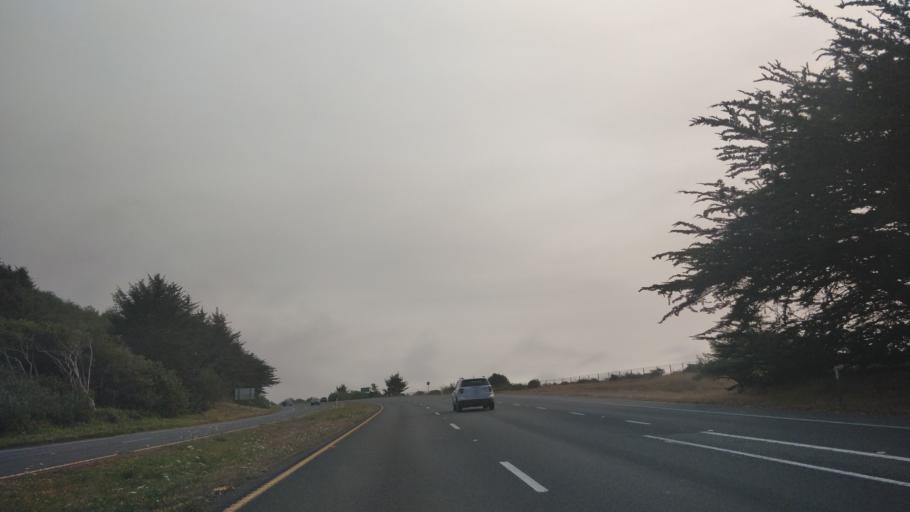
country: US
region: California
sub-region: Humboldt County
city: Westhaven-Moonstone
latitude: 41.0115
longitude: -124.1091
